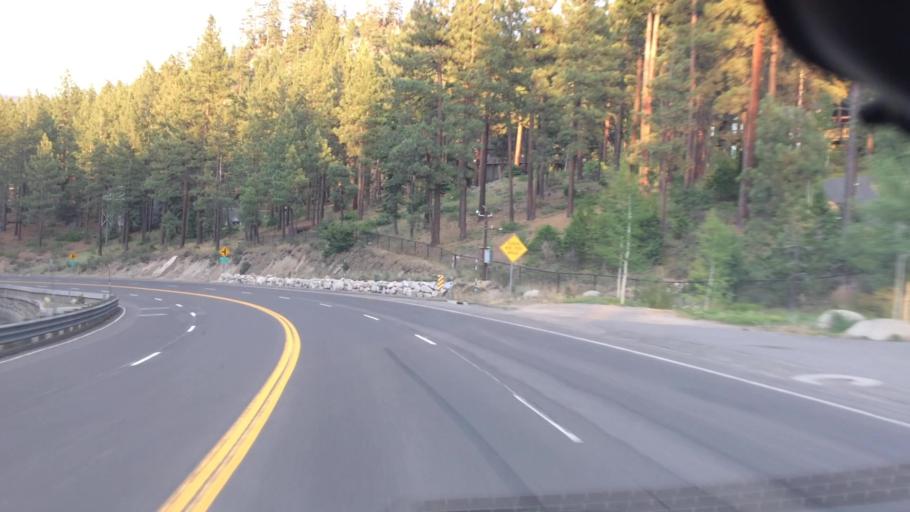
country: US
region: Nevada
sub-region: Douglas County
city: Kingsbury
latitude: 39.0024
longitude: -119.9500
